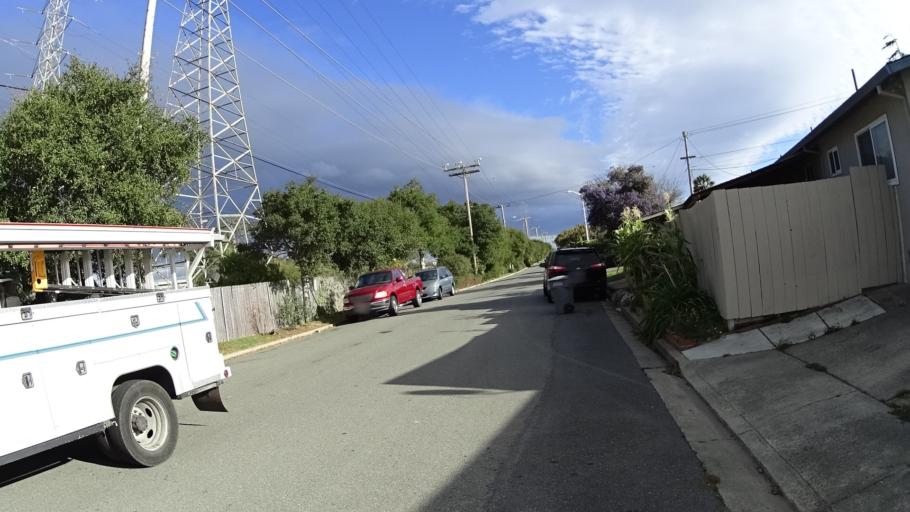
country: US
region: California
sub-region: San Mateo County
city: Millbrae
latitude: 37.6098
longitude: -122.3937
